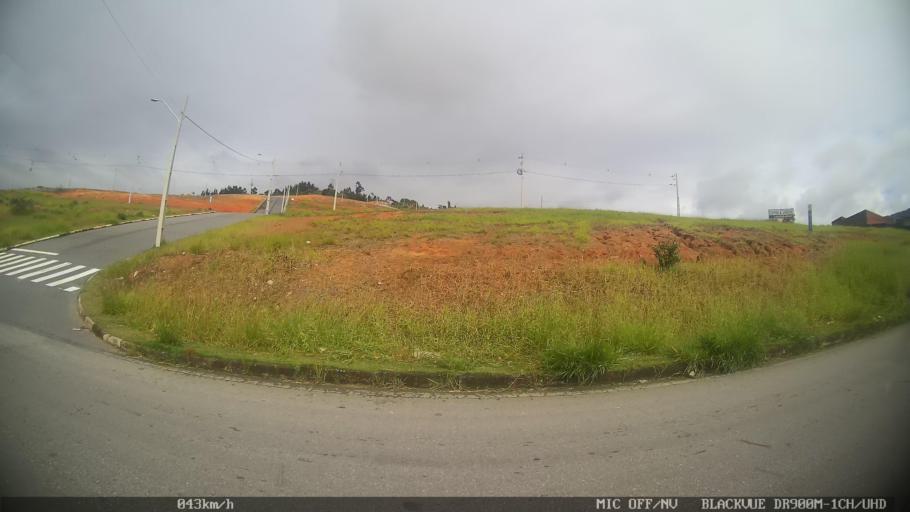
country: BR
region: Santa Catarina
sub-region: Biguacu
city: Biguacu
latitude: -27.5276
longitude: -48.6534
